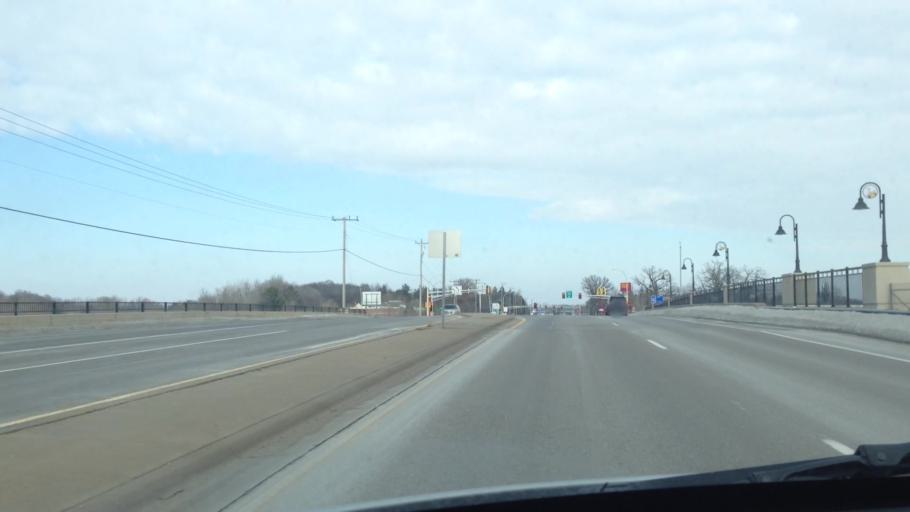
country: US
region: Minnesota
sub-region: Anoka County
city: Lino Lakes
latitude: 45.1795
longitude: -93.1133
